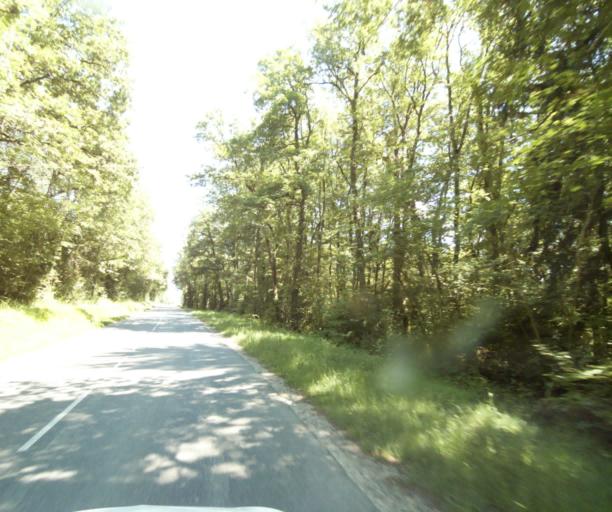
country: FR
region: Rhone-Alpes
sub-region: Departement de la Haute-Savoie
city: Loisin
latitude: 46.2676
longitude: 6.3229
